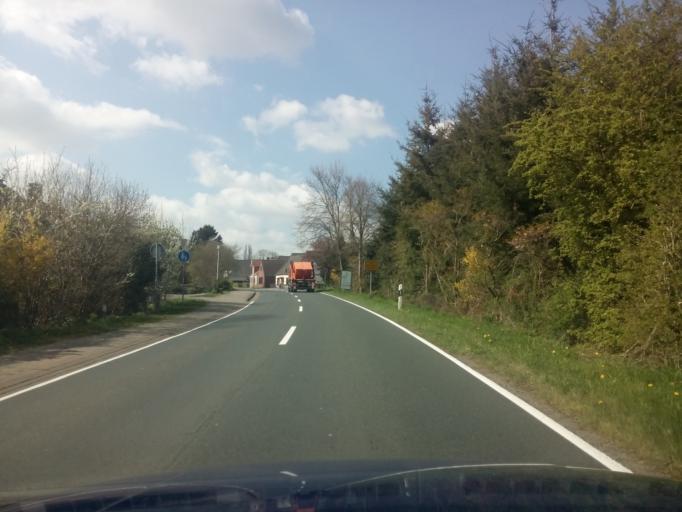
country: DE
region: Lower Saxony
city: Osterholz-Scharmbeck
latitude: 53.2184
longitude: 8.8076
